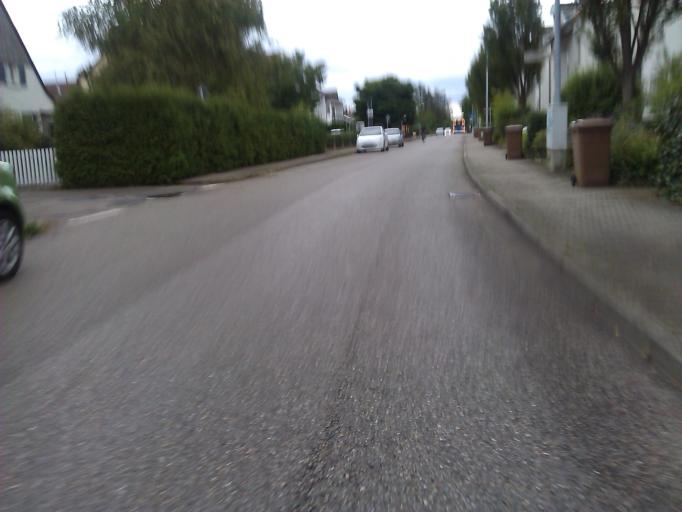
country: DE
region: Baden-Wuerttemberg
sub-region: Regierungsbezirk Stuttgart
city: Neckartailfingen
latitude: 48.6105
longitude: 9.2698
